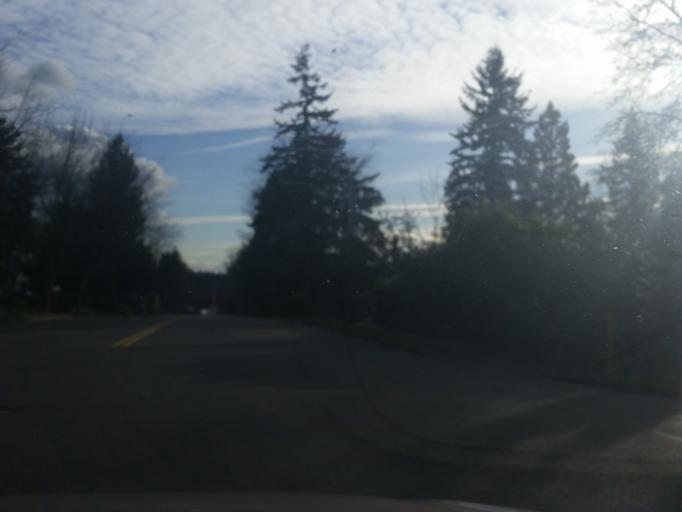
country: US
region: Washington
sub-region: King County
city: Shoreline
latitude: 47.7437
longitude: -122.3239
